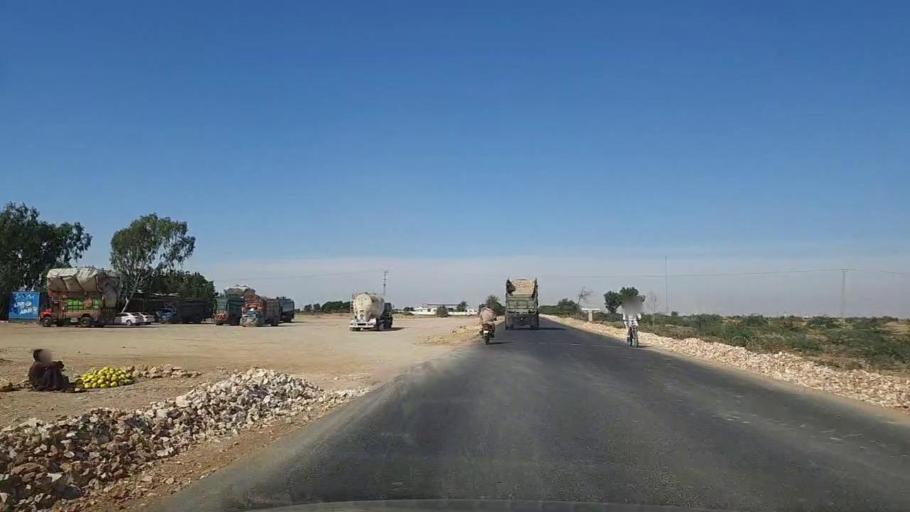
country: PK
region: Sindh
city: Kotri
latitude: 25.2640
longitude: 68.2207
